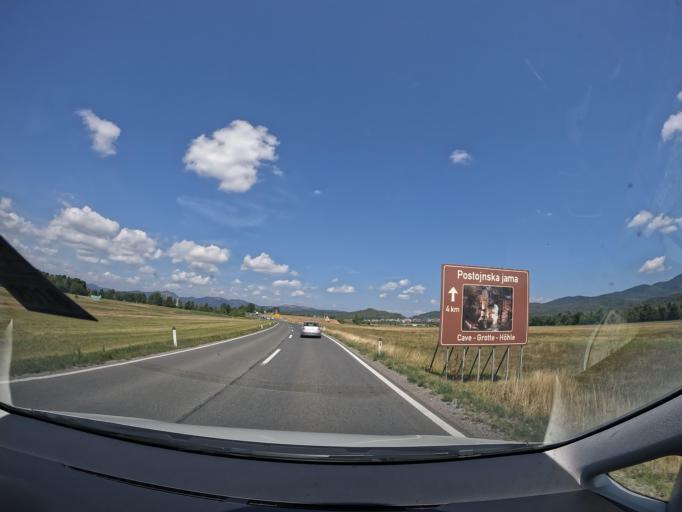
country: SI
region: Postojna
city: Postojna
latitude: 45.7554
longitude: 14.1964
